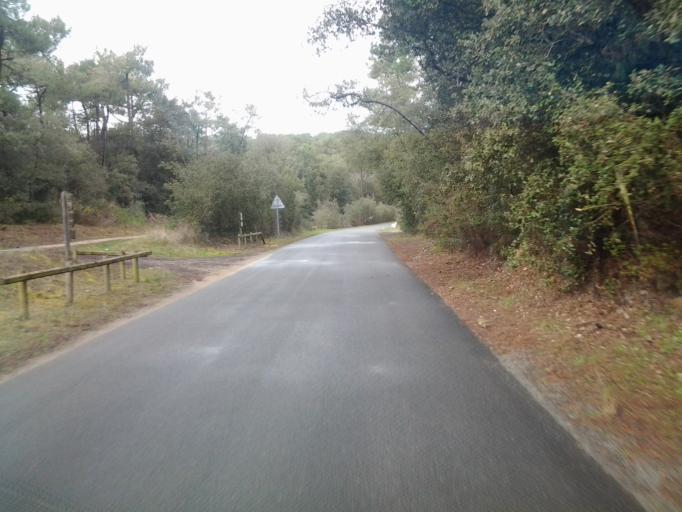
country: FR
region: Pays de la Loire
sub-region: Departement de la Vendee
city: La Tranche-sur-Mer
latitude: 46.3515
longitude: -1.4608
